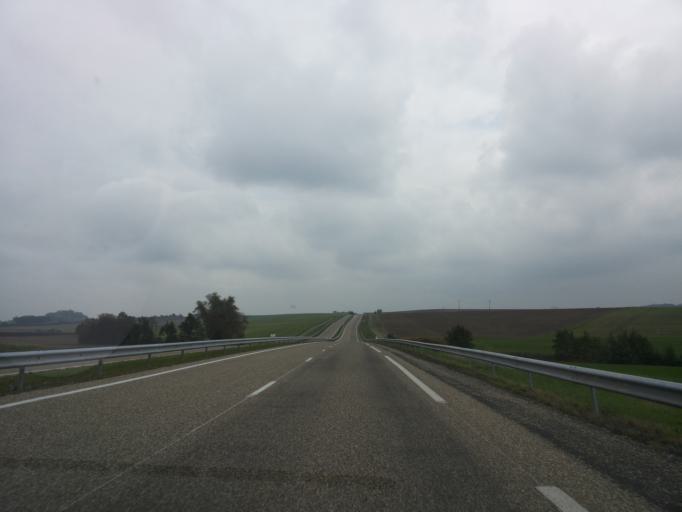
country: FR
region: Lorraine
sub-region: Departement de la Moselle
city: Dieuze
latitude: 48.7327
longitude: 6.6896
